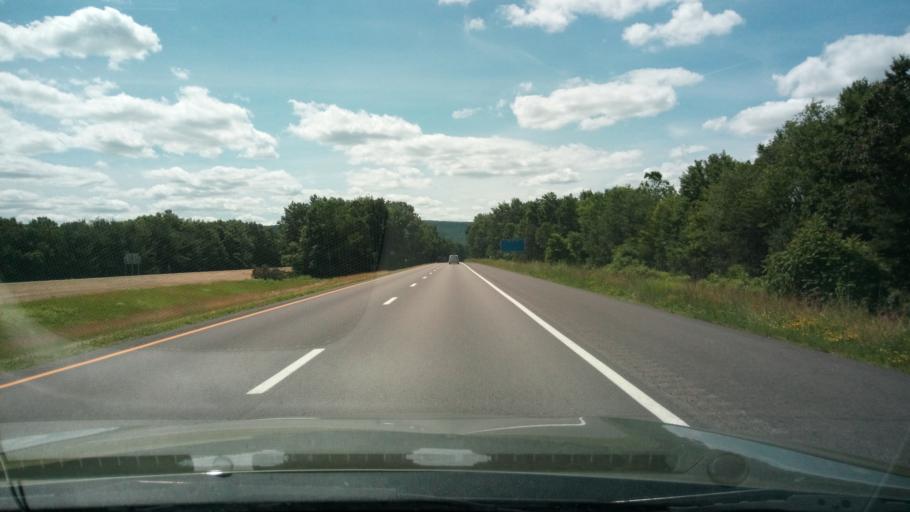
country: US
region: Pennsylvania
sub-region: Bradford County
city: South Waverly
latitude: 42.0015
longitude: -76.6116
